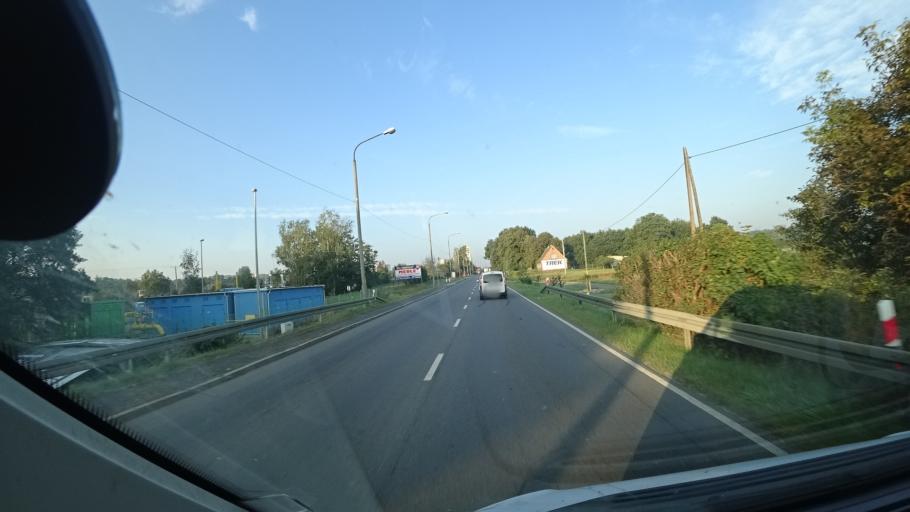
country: PL
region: Opole Voivodeship
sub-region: Powiat kedzierzynsko-kozielski
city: Kedzierzyn-Kozle
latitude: 50.3591
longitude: 18.2616
